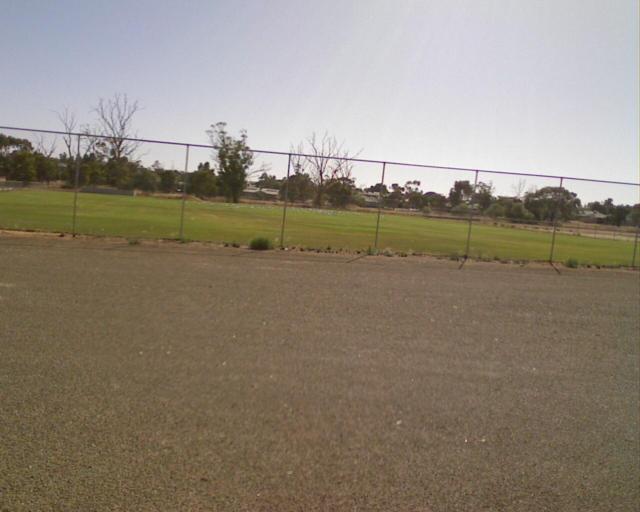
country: AU
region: Western Australia
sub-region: Wongan-Ballidu
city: Wongan Hills
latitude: -30.2751
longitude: 116.6569
